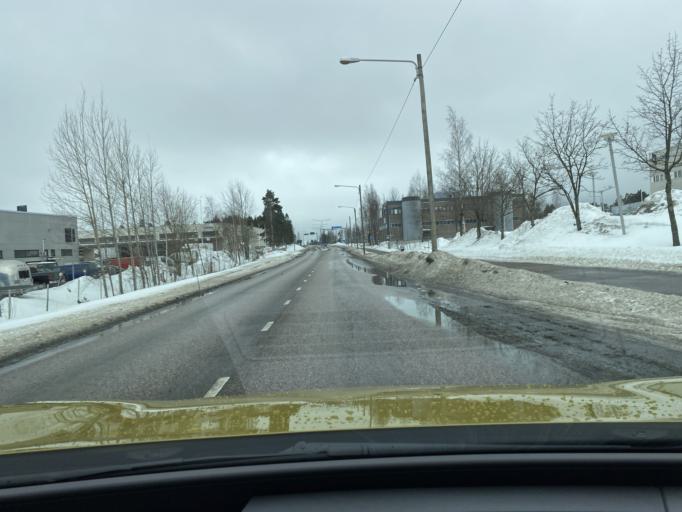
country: FI
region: Uusimaa
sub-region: Helsinki
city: Vantaa
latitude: 60.2997
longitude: 24.9413
